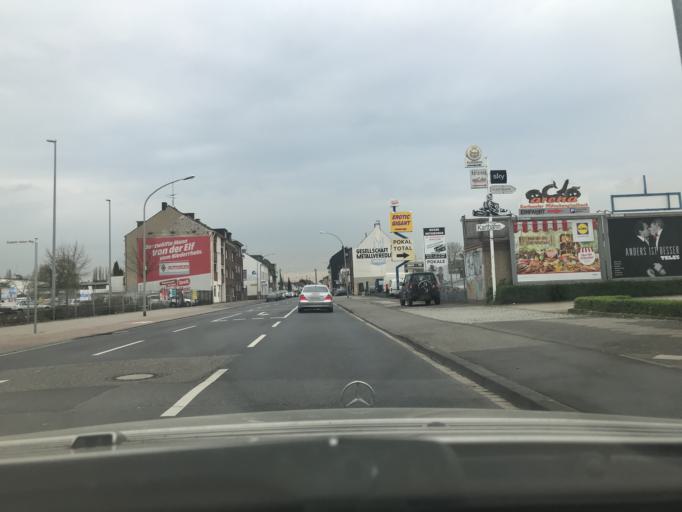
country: DE
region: North Rhine-Westphalia
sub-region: Regierungsbezirk Dusseldorf
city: Monchengladbach
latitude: 51.2057
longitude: 6.4582
